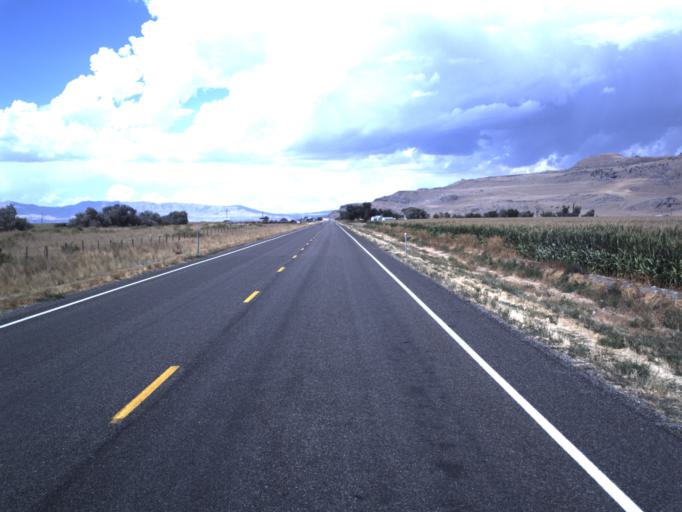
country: US
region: Utah
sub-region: Box Elder County
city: Honeyville
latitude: 41.5674
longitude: -112.1885
